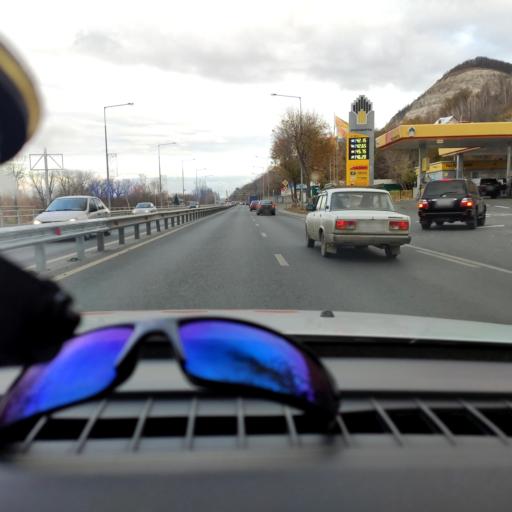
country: RU
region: Samara
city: Volzhskiy
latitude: 53.3853
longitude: 50.1635
